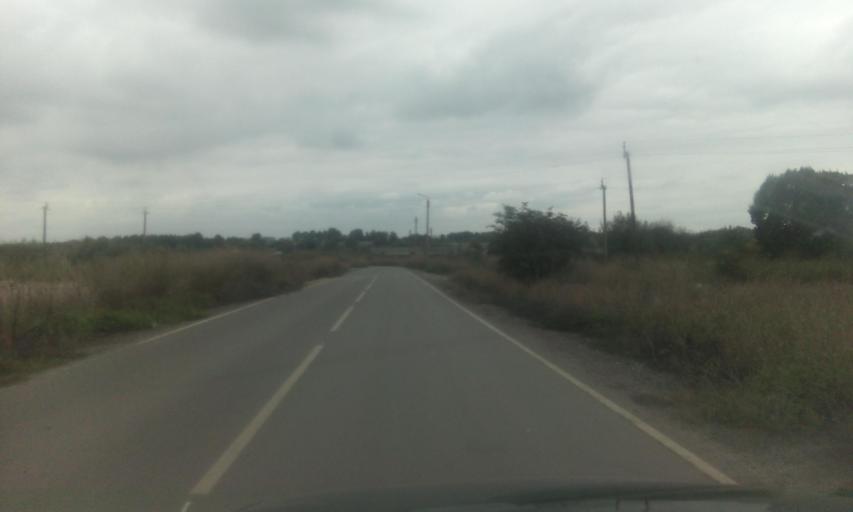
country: RU
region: Tula
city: Dubovka
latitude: 53.9389
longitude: 38.0301
